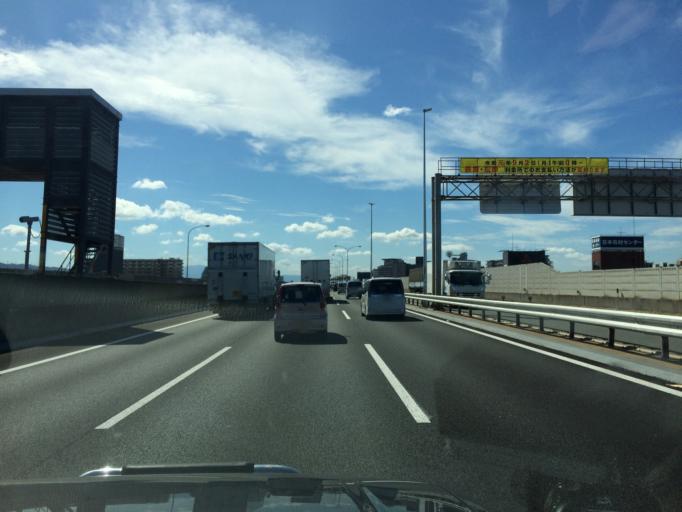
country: JP
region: Osaka
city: Daitocho
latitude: 34.6739
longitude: 135.5980
